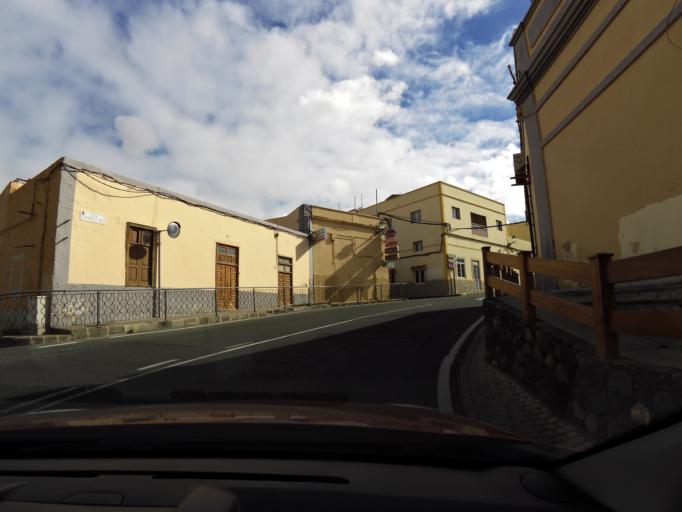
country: ES
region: Canary Islands
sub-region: Provincia de Las Palmas
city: Aguimes
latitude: 27.9072
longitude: -15.4434
